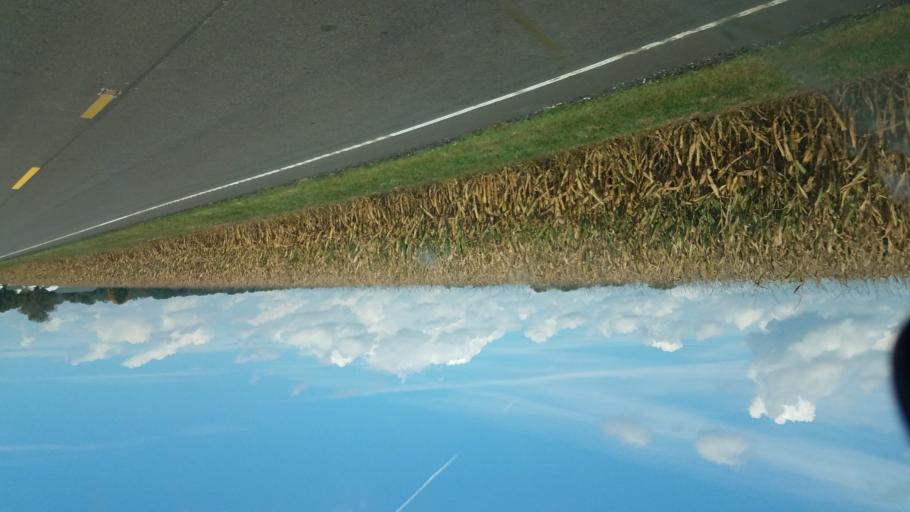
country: US
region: Ohio
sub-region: Knox County
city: Fredericktown
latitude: 40.4638
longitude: -82.6189
